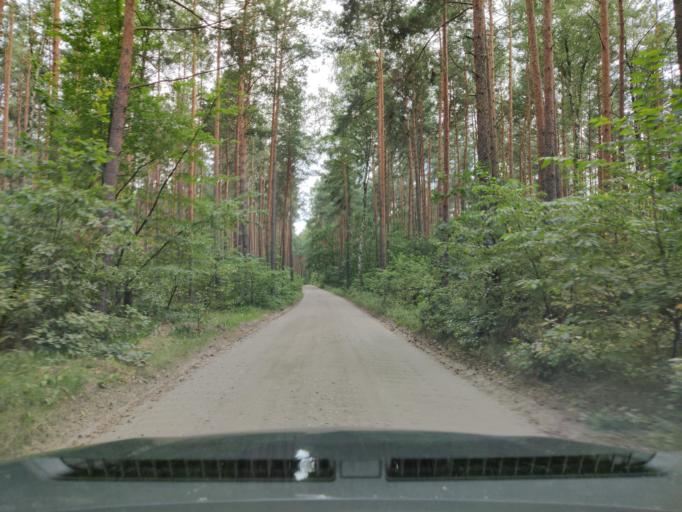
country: PL
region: Masovian Voivodeship
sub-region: Powiat pultuski
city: Pultusk
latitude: 52.7511
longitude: 21.1411
